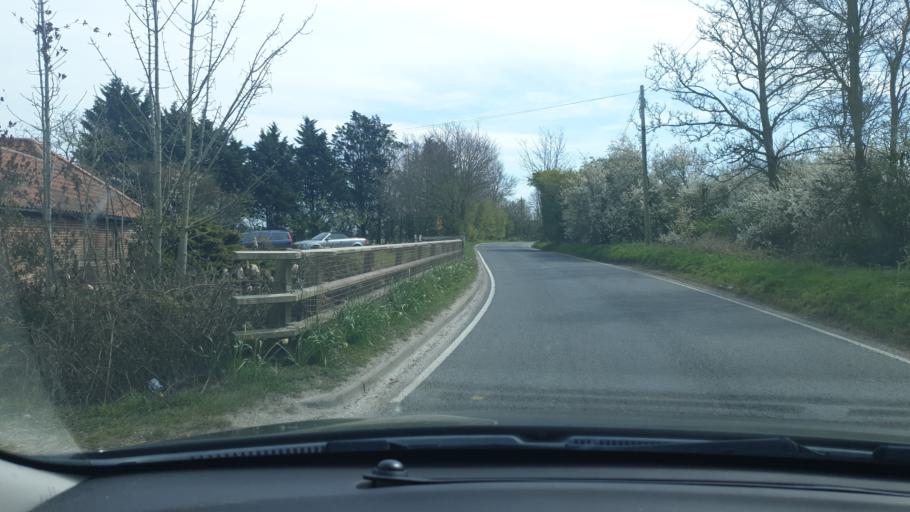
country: GB
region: England
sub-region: Essex
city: Little Clacton
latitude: 51.9092
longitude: 1.1697
